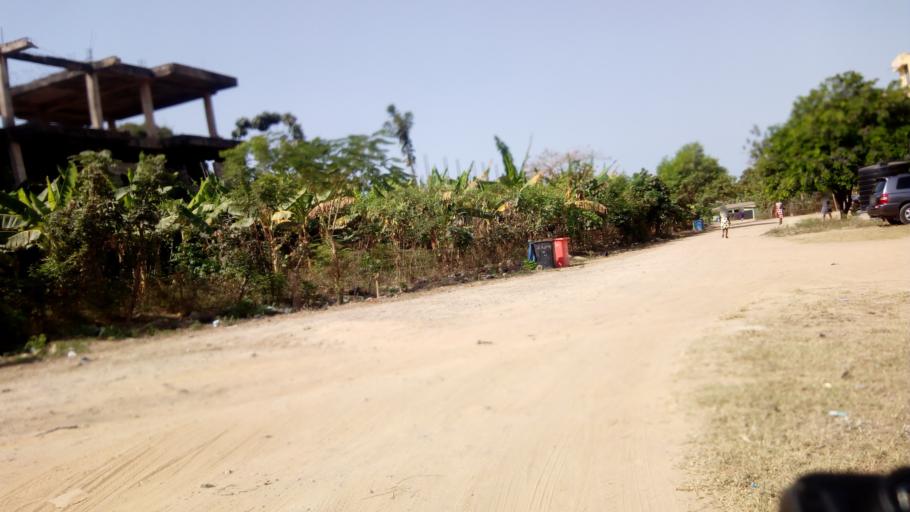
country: GH
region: Central
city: Cape Coast
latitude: 5.1215
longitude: -1.2695
